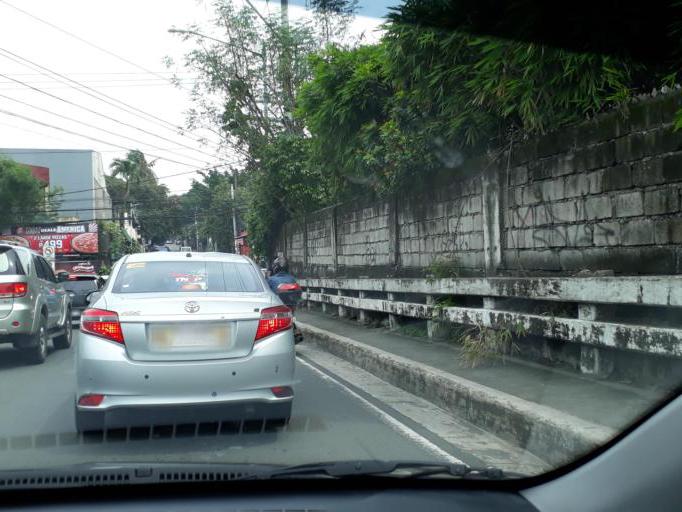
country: PH
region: Metro Manila
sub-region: Quezon City
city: Quezon City
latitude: 14.6292
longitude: 121.0559
